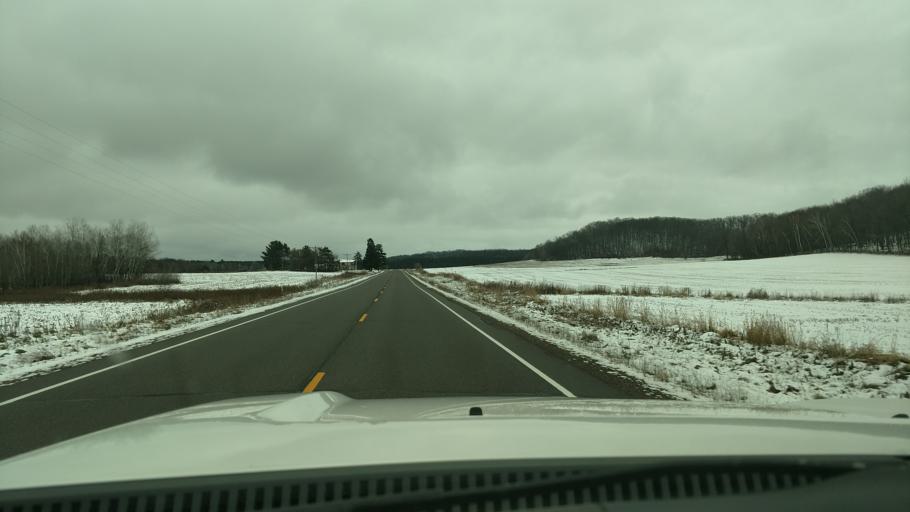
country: US
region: Wisconsin
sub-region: Dunn County
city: Colfax
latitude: 45.1390
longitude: -91.7628
